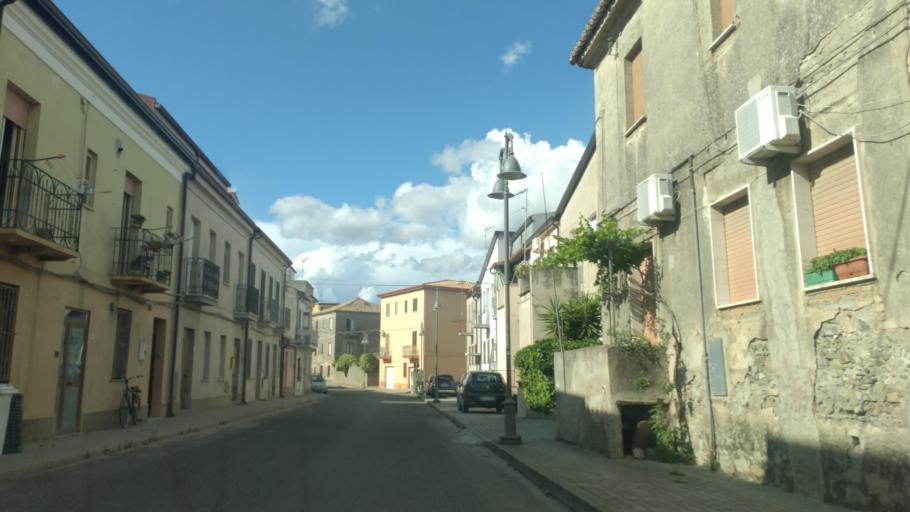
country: IT
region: Calabria
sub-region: Provincia di Catanzaro
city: Staletti
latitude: 38.7630
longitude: 16.5403
